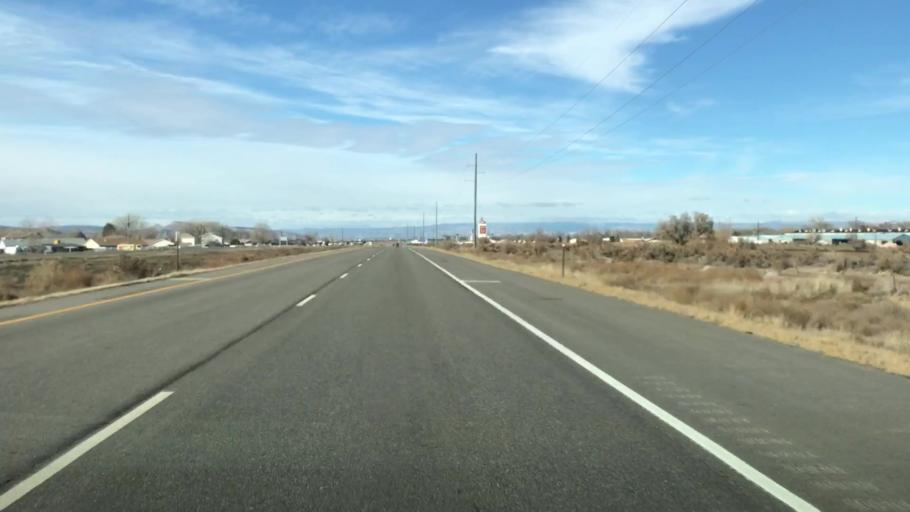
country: US
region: Colorado
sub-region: Mesa County
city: Fruita
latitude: 39.1481
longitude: -108.7212
